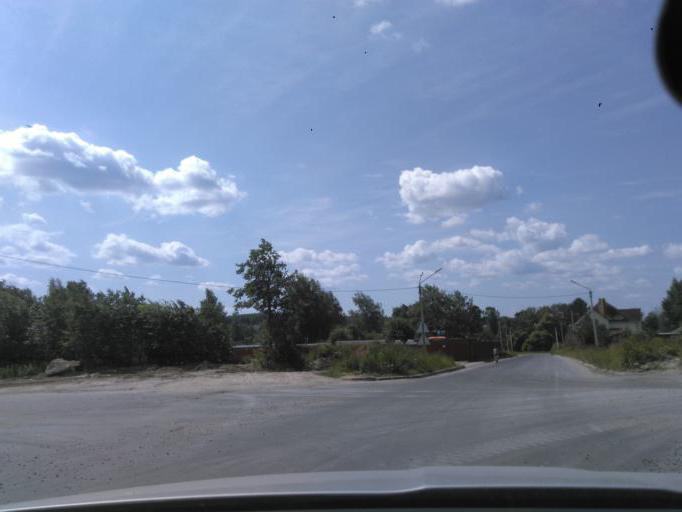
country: RU
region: Moskovskaya
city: Solnechnogorsk
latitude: 56.1661
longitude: 36.9780
